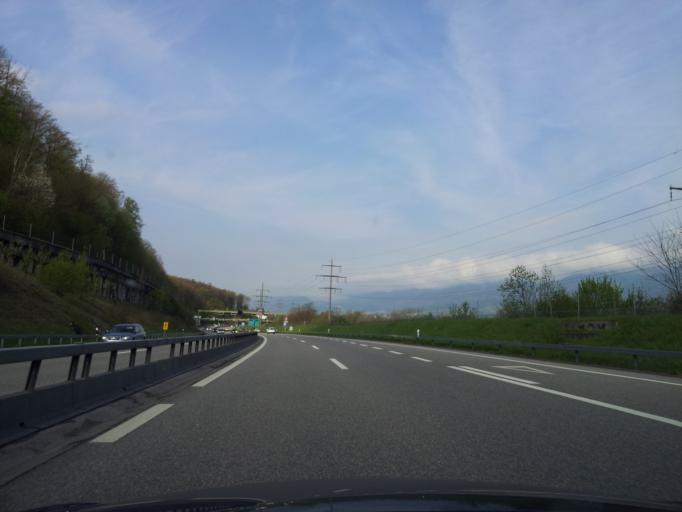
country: CH
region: Solothurn
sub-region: Bezirk Solothurn
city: Solothurn
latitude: 47.1957
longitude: 7.5254
